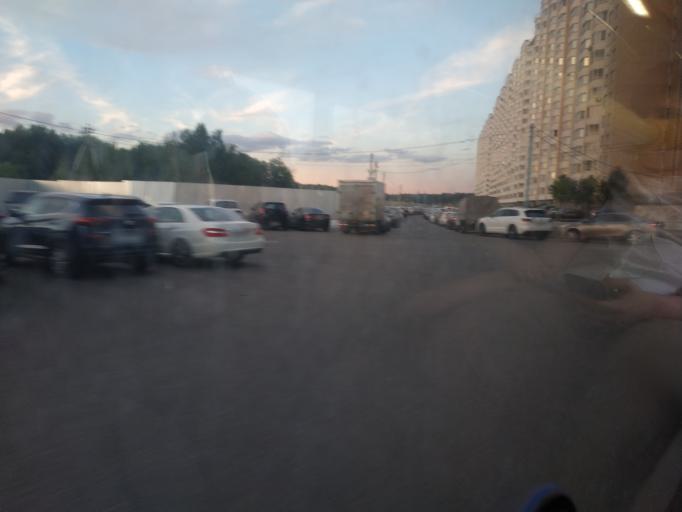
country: RU
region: Moskovskaya
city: Moskovskiy
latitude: 55.6059
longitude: 37.3633
